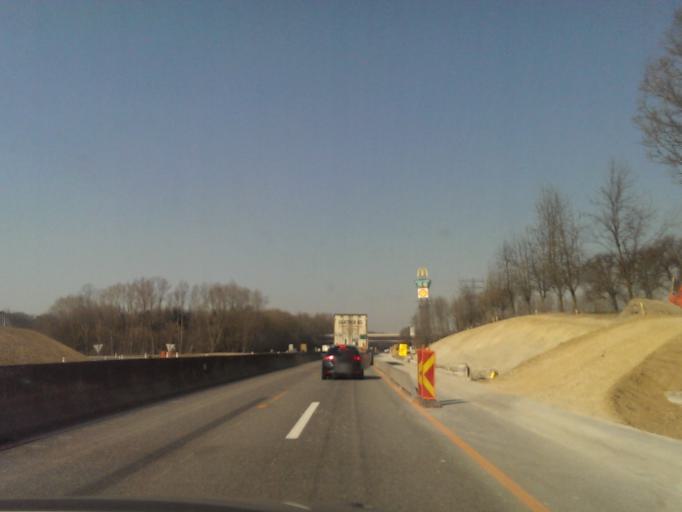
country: AT
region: Upper Austria
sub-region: Politischer Bezirk Vocklabruck
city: Wolfsegg am Hausruck
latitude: 48.1967
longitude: 13.6438
